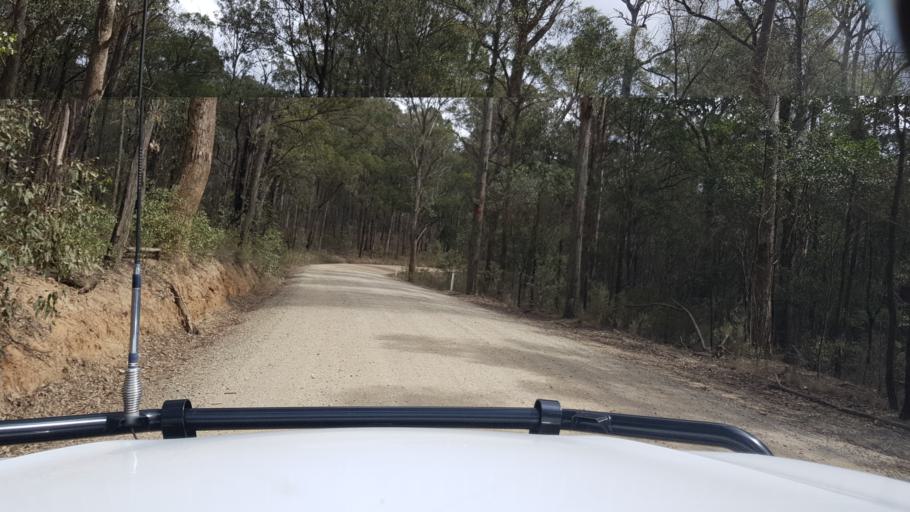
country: AU
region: Victoria
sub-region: East Gippsland
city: Bairnsdale
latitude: -37.7000
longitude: 147.5818
